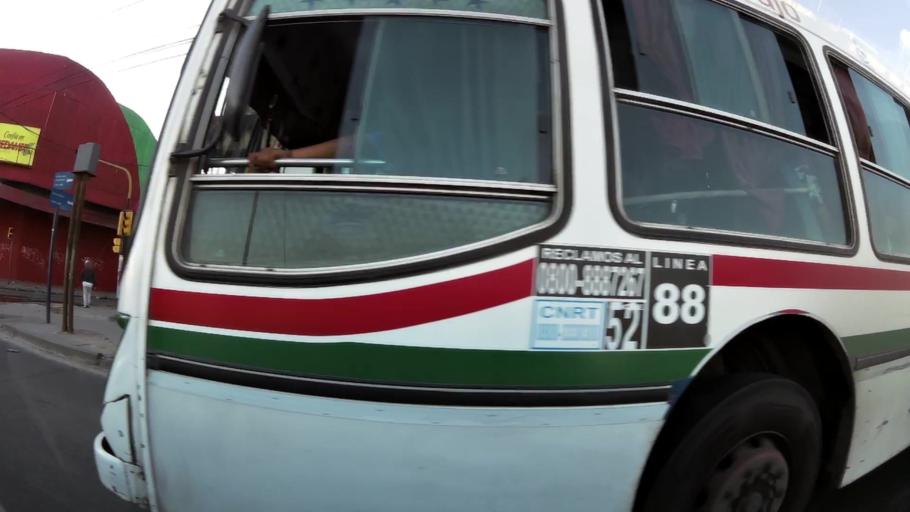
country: AR
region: Buenos Aires
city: Pontevedra
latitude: -34.7425
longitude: -58.6078
